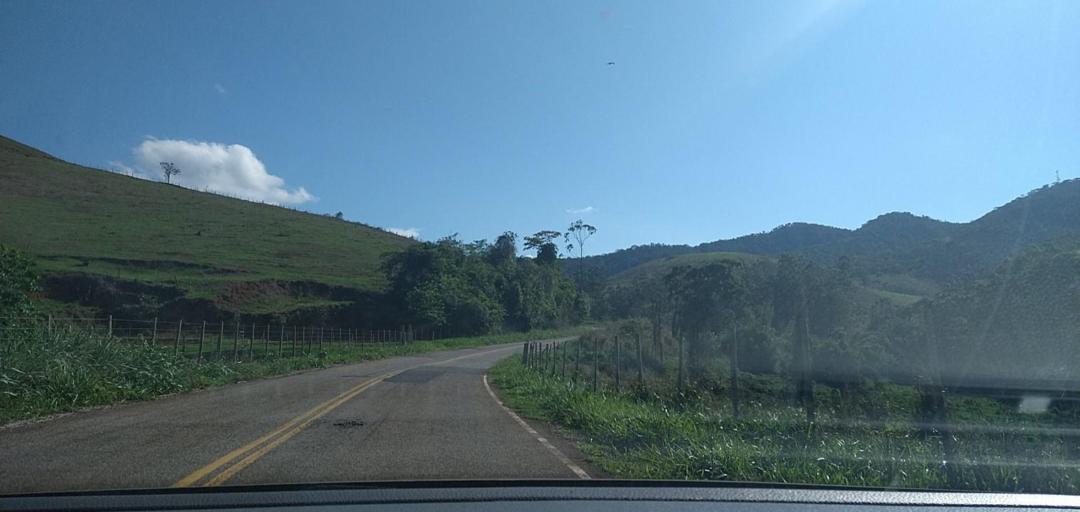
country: BR
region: Minas Gerais
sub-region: Alvinopolis
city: Alvinopolis
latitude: -20.1859
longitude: -42.9361
